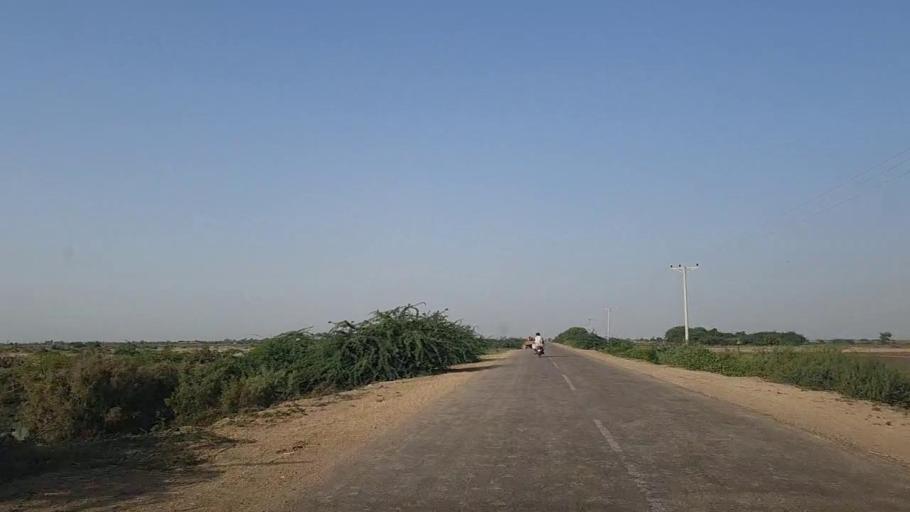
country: PK
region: Sindh
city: Mirpur Batoro
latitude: 24.6081
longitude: 68.4026
